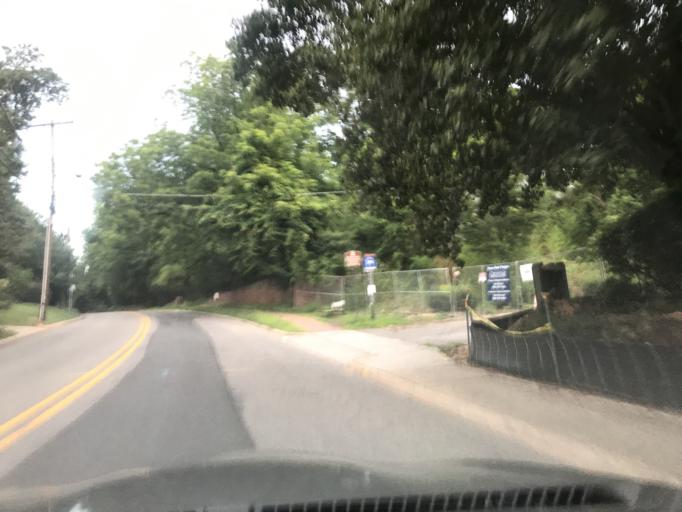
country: US
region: North Carolina
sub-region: Orange County
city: Chapel Hill
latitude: 35.9201
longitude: -79.0517
